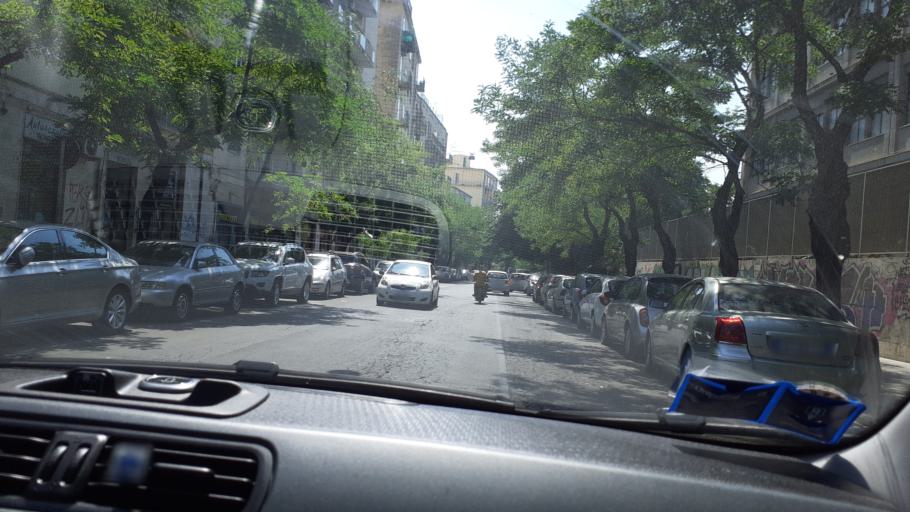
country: IT
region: Sicily
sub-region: Catania
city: Catania
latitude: 37.5101
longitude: 15.0752
